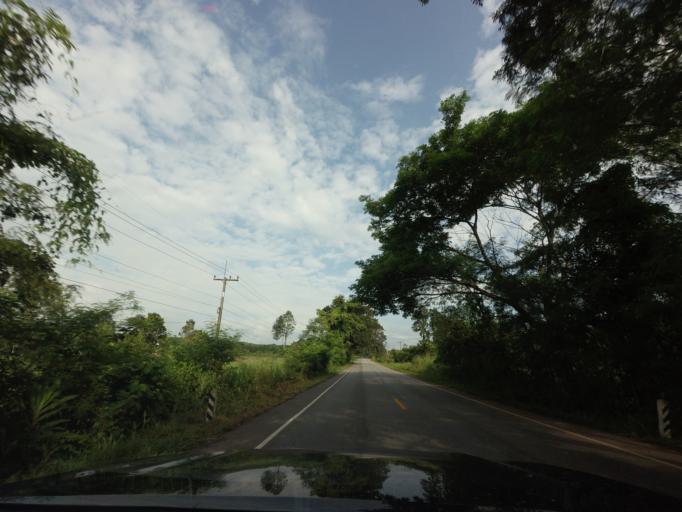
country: TH
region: Nong Khai
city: Pho Tak
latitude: 17.7958
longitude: 102.3533
